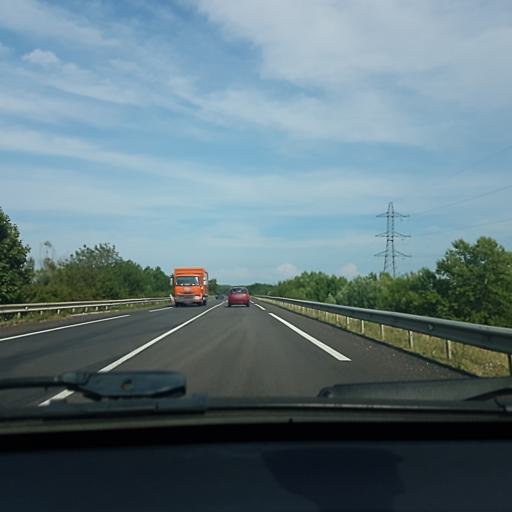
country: FR
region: Bourgogne
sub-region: Departement de Saone-et-Loire
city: Saint-Marcel
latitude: 46.7615
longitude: 4.8795
